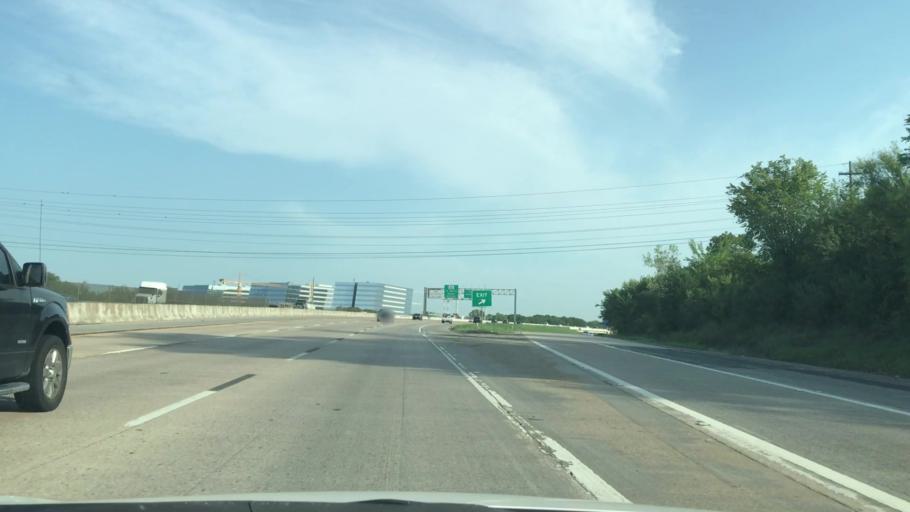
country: US
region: Texas
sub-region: Tarrant County
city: Euless
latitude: 32.8185
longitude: -97.0596
